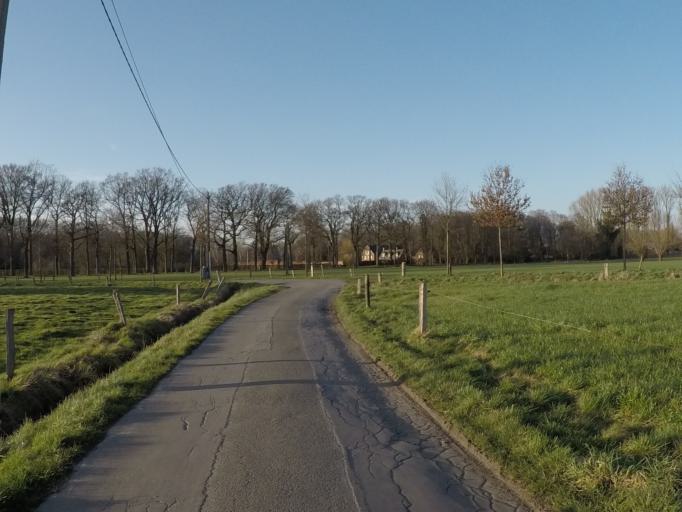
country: BE
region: Flanders
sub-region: Provincie Antwerpen
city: Aartselaar
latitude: 51.1381
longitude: 4.4151
